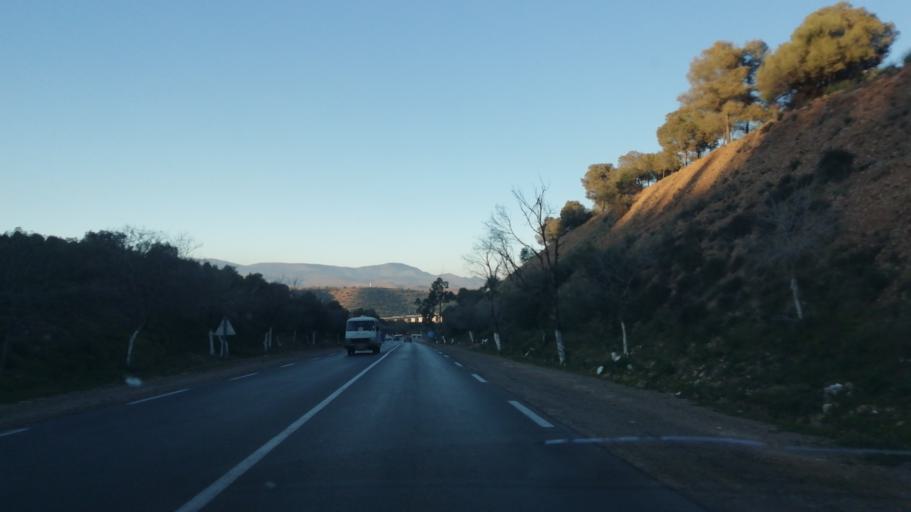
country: DZ
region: Tlemcen
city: Nedroma
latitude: 34.8765
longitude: -1.6682
